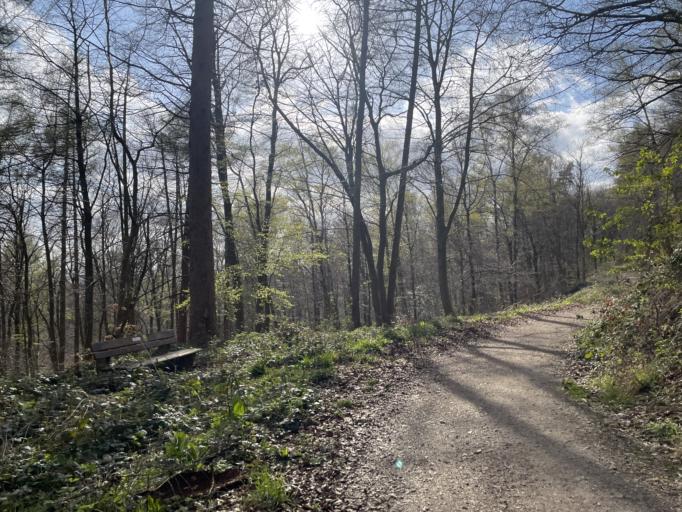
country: DE
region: North Rhine-Westphalia
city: Porta Westfalica
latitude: 52.2385
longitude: 8.9467
